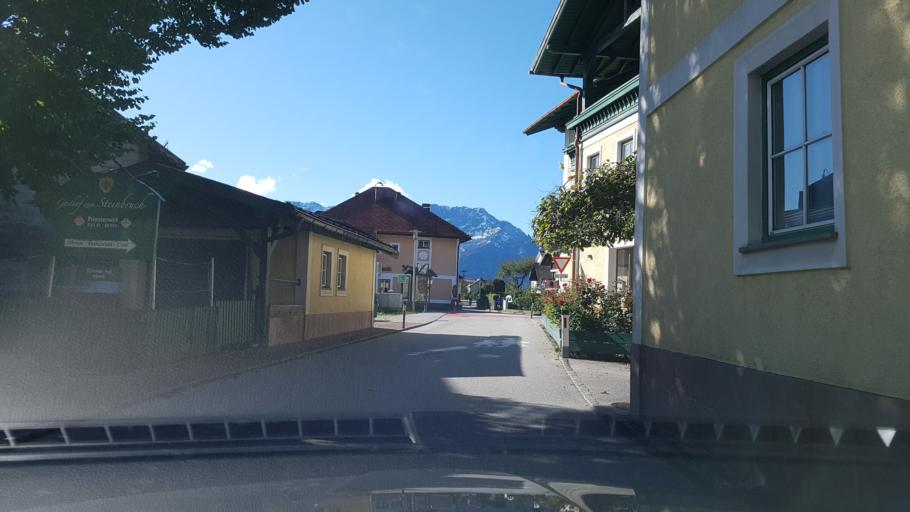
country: AT
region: Salzburg
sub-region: Politischer Bezirk Hallein
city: Adnet
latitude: 47.6966
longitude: 13.1311
